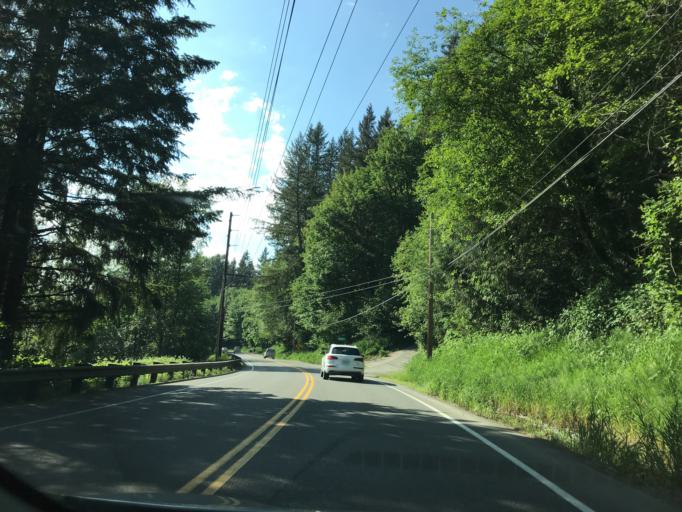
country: US
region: Washington
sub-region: King County
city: Mirrormont
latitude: 47.4606
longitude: -122.0079
